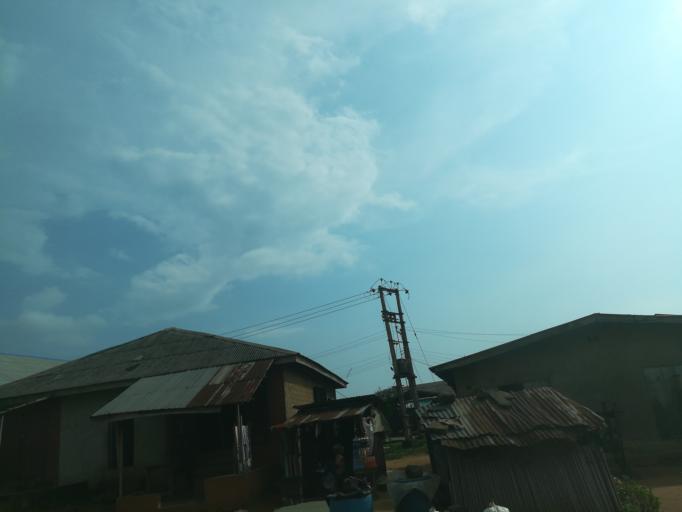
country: NG
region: Lagos
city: Ikorodu
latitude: 6.6674
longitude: 3.6674
